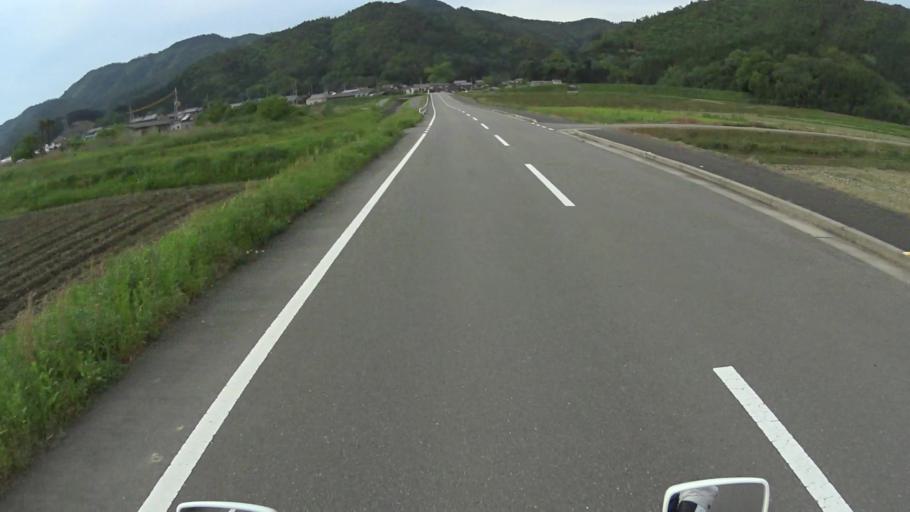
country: JP
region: Kyoto
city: Kameoka
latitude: 35.0930
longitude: 135.5478
